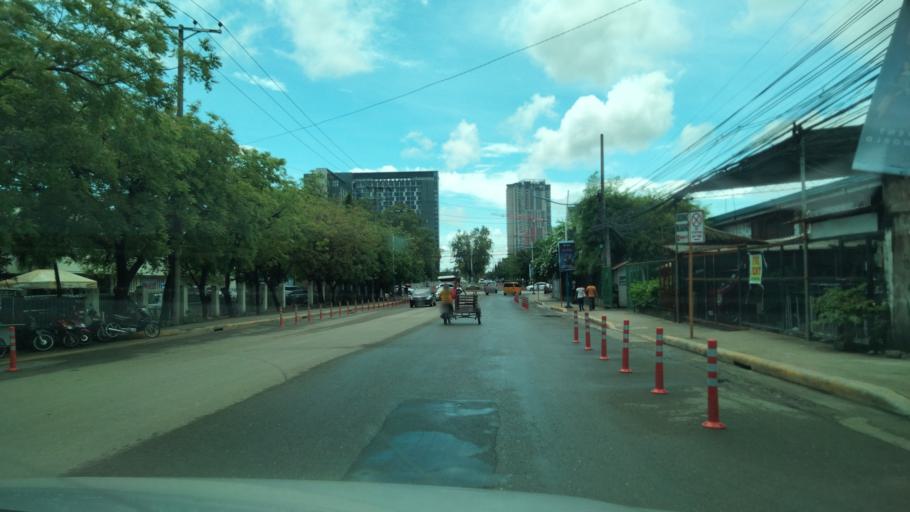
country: PH
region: Central Visayas
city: Mandaue City
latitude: 10.3275
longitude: 123.9340
